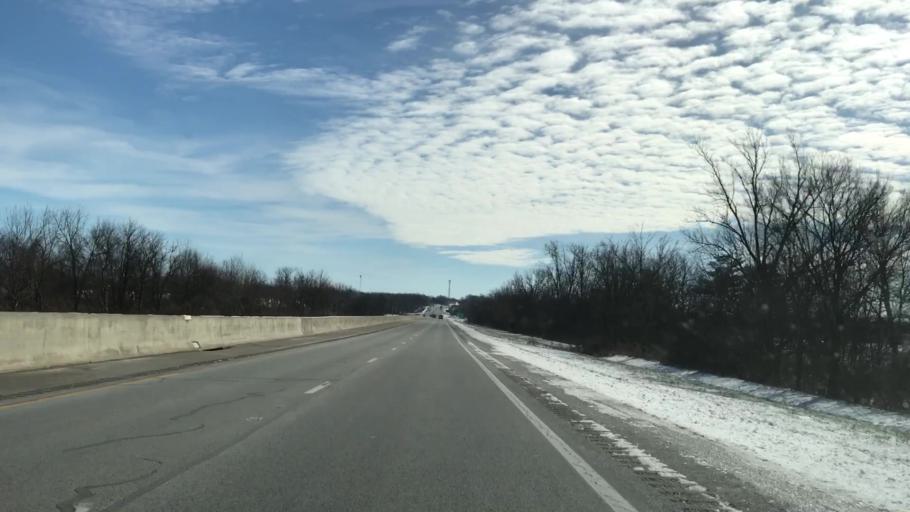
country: US
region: Kentucky
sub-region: Hardin County
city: Elizabethtown
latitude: 37.6958
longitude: -85.8781
